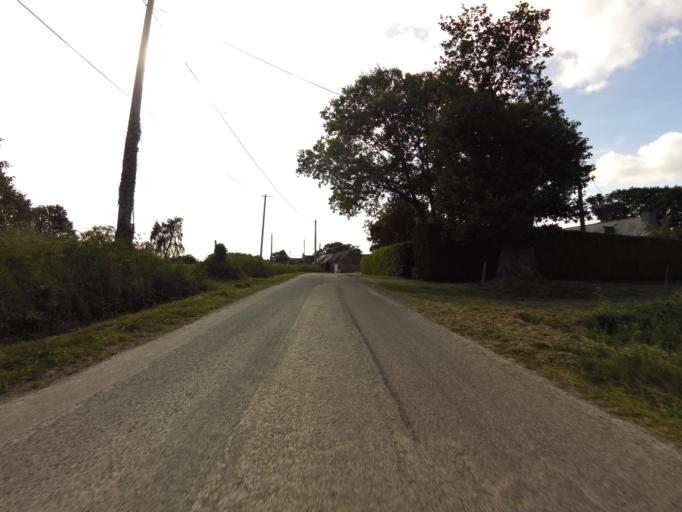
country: FR
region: Brittany
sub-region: Departement du Morbihan
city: Molac
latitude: 47.7129
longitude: -2.4136
